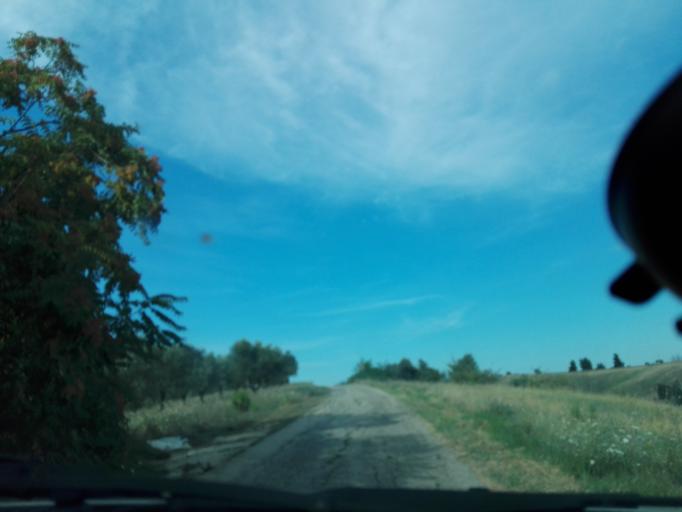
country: IT
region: Abruzzo
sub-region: Provincia di Pescara
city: Cappelle sul Tavo
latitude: 42.4526
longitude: 14.1069
